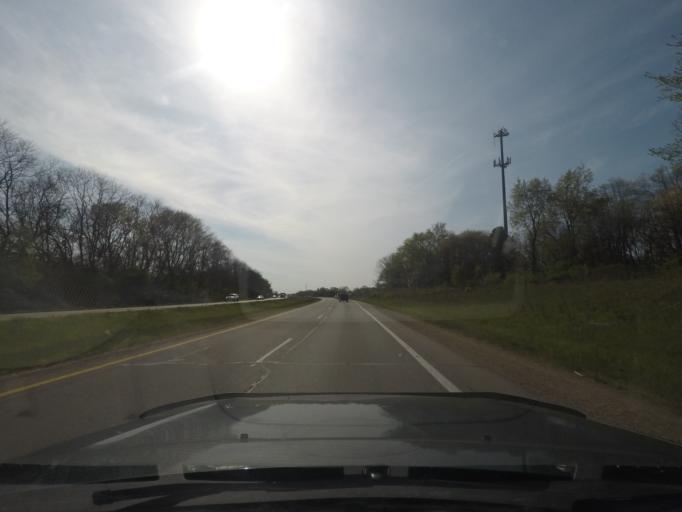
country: US
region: Michigan
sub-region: Berrien County
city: Niles
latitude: 41.8051
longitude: -86.2953
